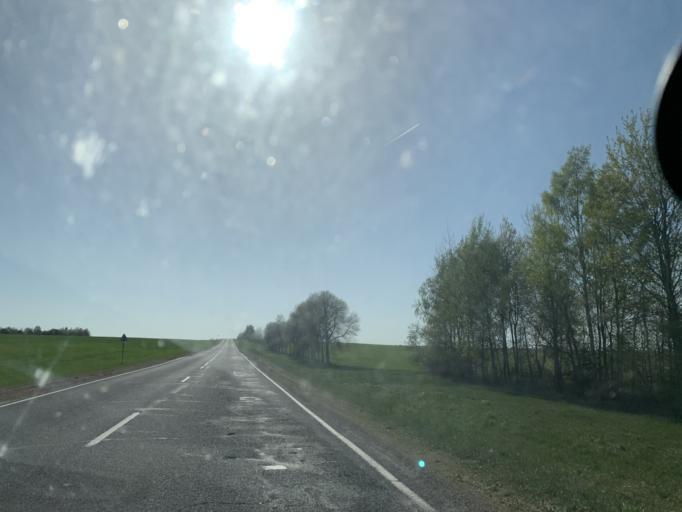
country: BY
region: Minsk
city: Nyasvizh
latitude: 53.2452
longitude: 26.8724
